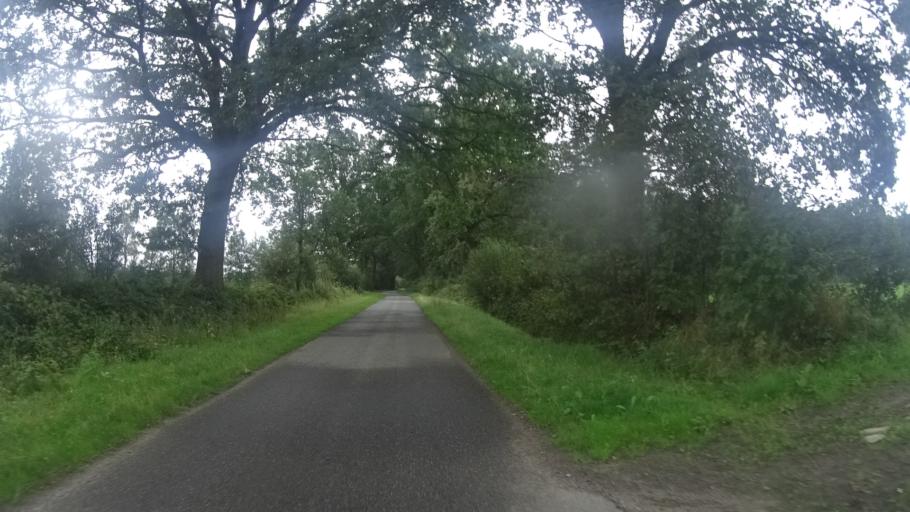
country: DE
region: Schleswig-Holstein
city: Bevern
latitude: 53.7615
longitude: 9.7925
